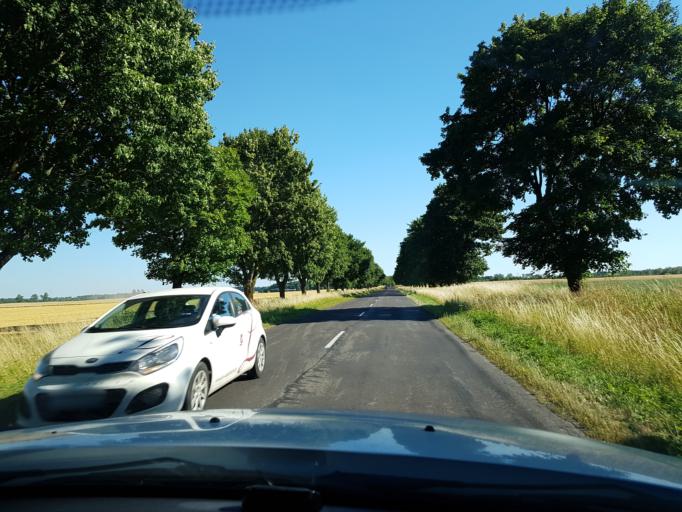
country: PL
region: West Pomeranian Voivodeship
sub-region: Powiat lobeski
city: Lobez
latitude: 53.6933
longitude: 15.6069
